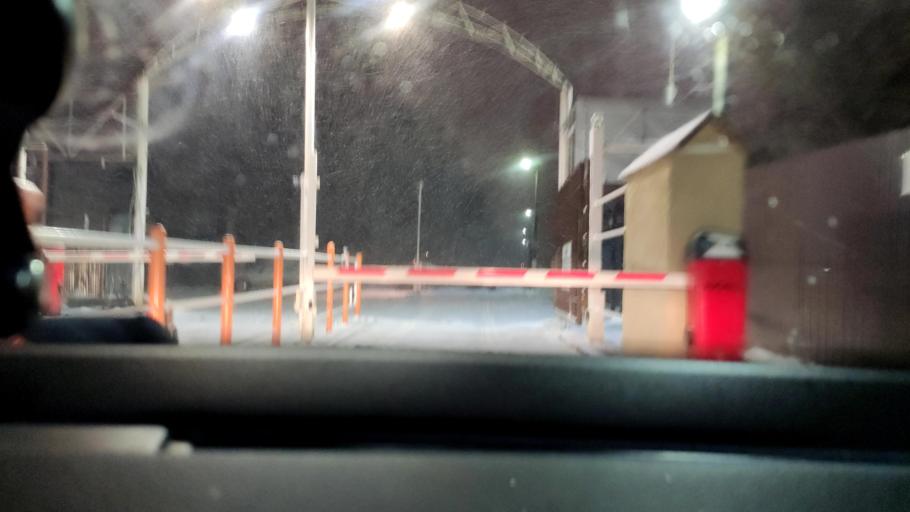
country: RU
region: Moskovskaya
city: Mosrentgen
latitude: 55.6281
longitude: 37.4586
